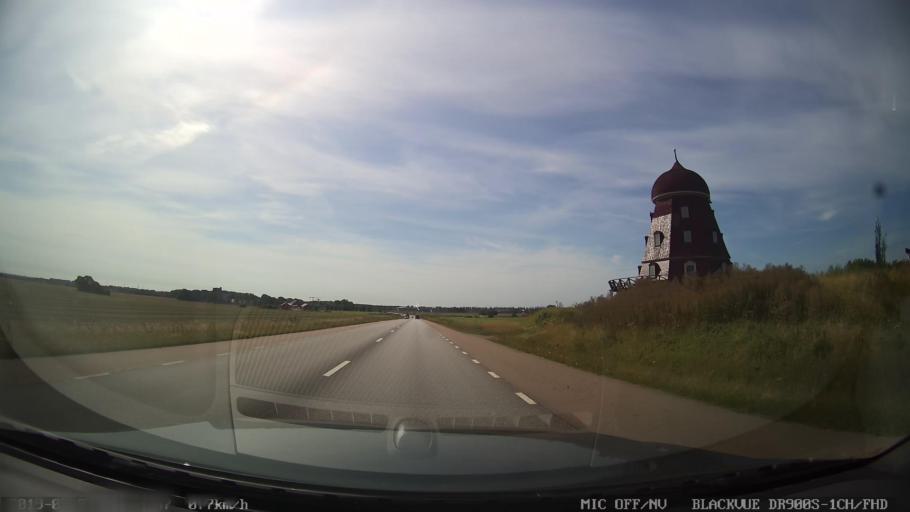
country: SE
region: Skane
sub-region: Helsingborg
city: Glumslov
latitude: 55.9138
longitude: 12.8233
